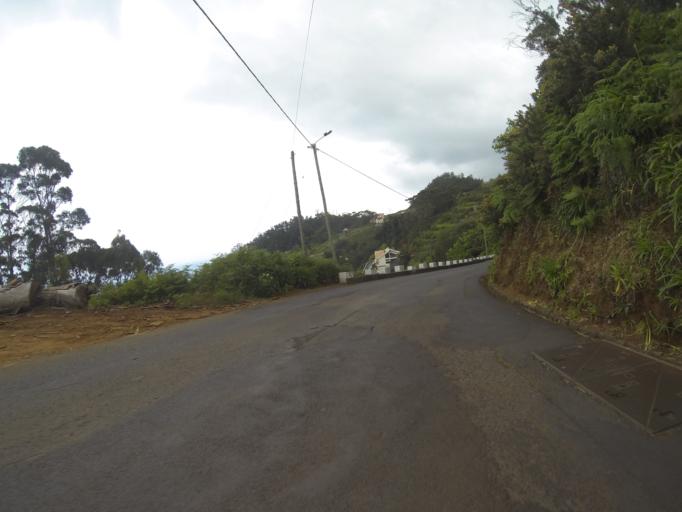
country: PT
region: Madeira
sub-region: Porto Moniz
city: Porto Moniz
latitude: 32.8608
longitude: -17.1711
